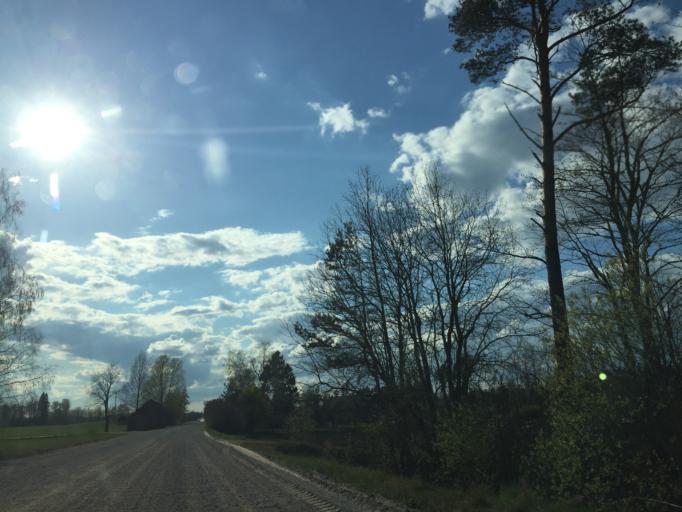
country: LV
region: Beverina
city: Murmuiza
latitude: 57.3982
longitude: 25.4836
